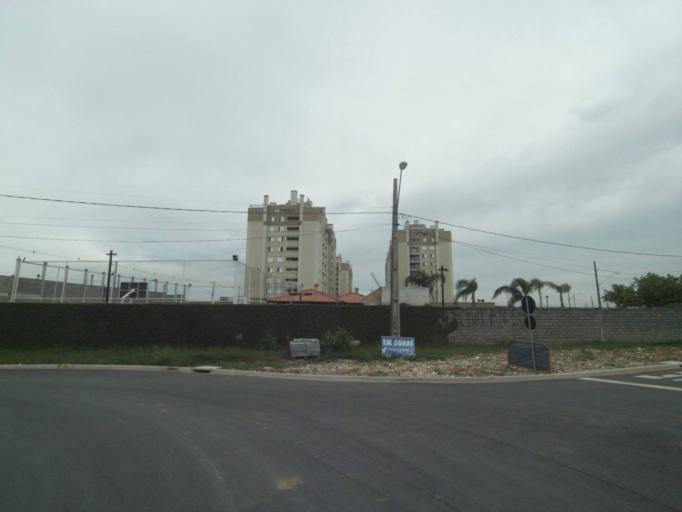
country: BR
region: Parana
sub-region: Pinhais
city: Pinhais
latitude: -25.4291
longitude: -49.2011
